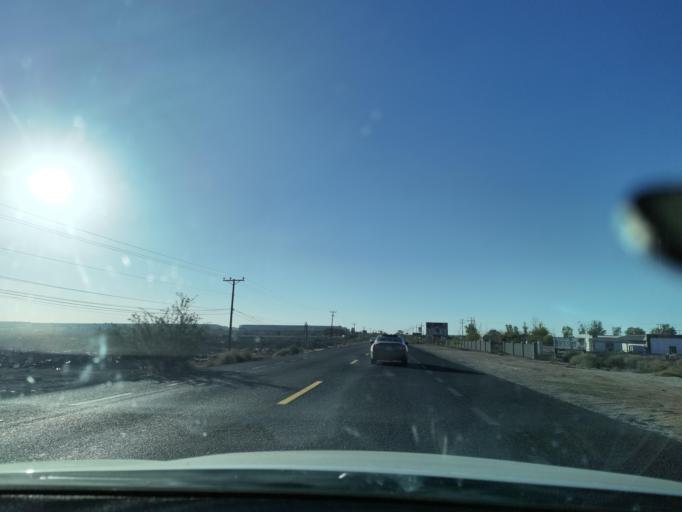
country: MX
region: Baja California
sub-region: Mexicali
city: Islas Agrarias Grupo A
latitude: 32.6380
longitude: -115.2894
